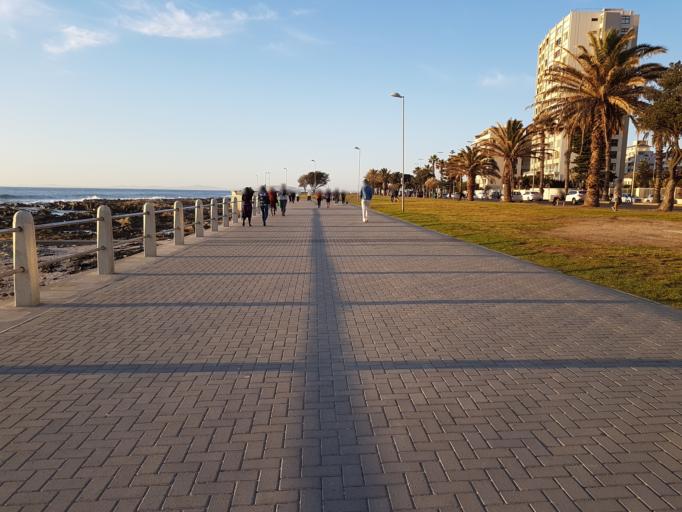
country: ZA
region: Western Cape
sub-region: City of Cape Town
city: Cape Town
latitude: -33.9131
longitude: 18.3878
